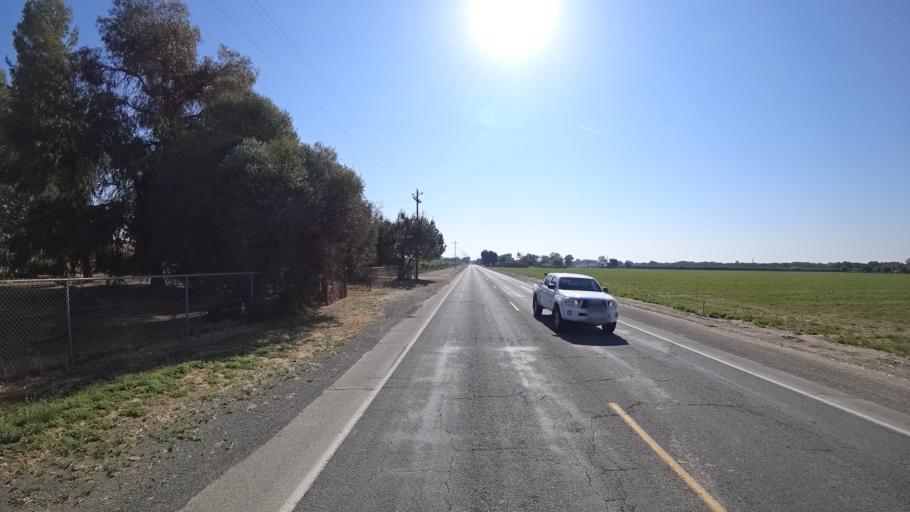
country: US
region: California
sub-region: Kings County
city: Lemoore
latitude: 36.3440
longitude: -119.8549
